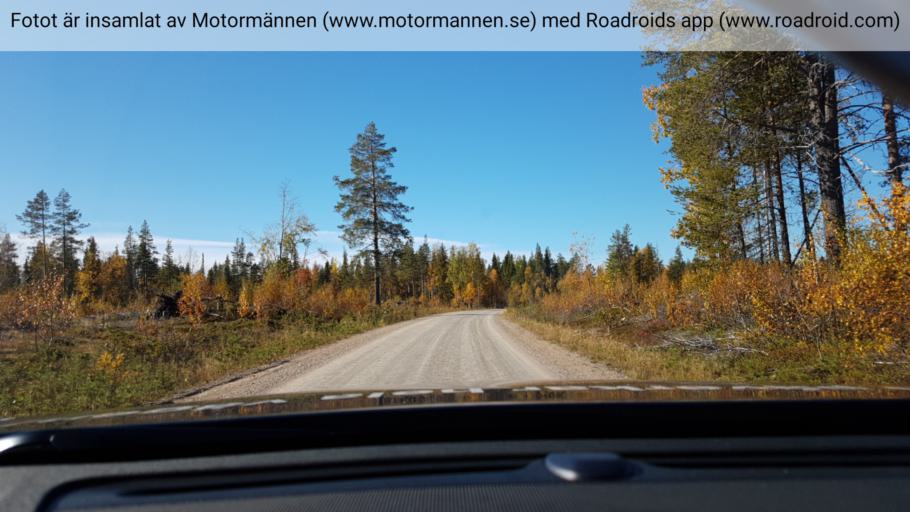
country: SE
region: Norrbotten
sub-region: Gallivare Kommun
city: Gaellivare
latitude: 66.6560
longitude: 20.9764
